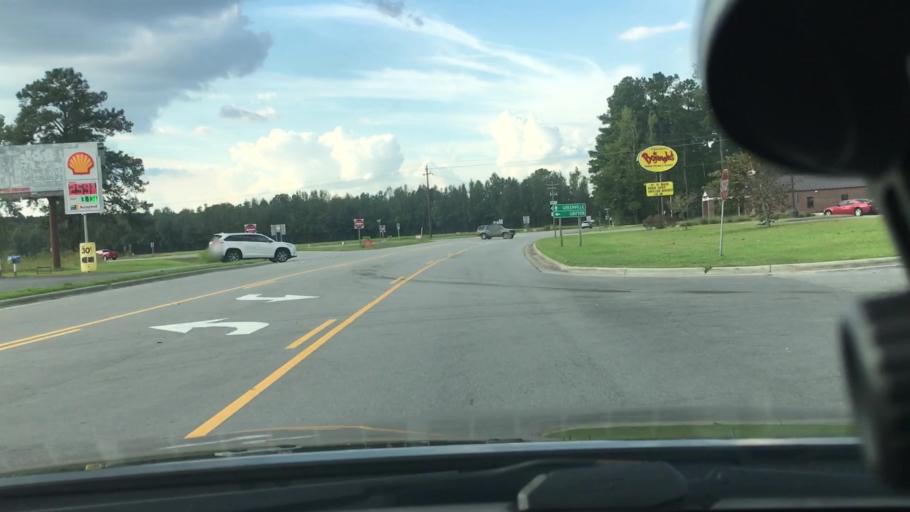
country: US
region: North Carolina
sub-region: Craven County
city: Vanceboro
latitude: 35.3116
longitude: -77.1606
